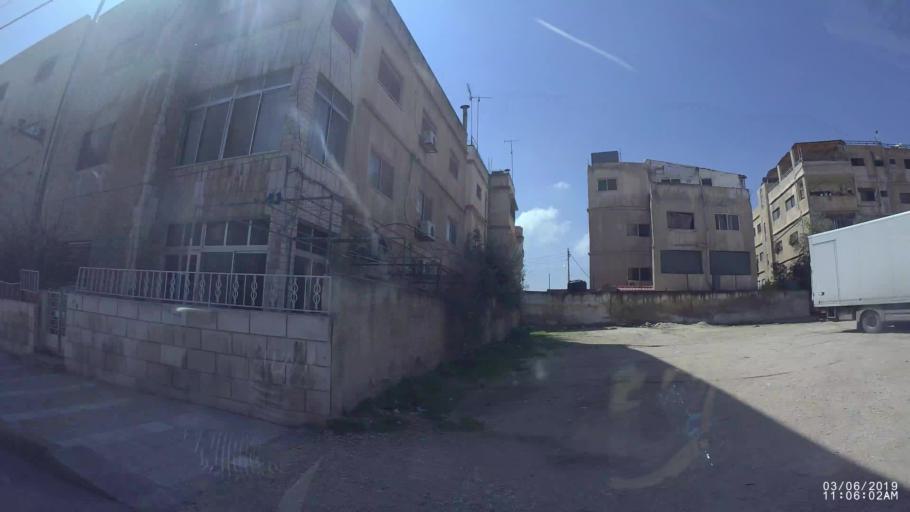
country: JO
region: Amman
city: Amman
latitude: 31.9765
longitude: 35.9882
